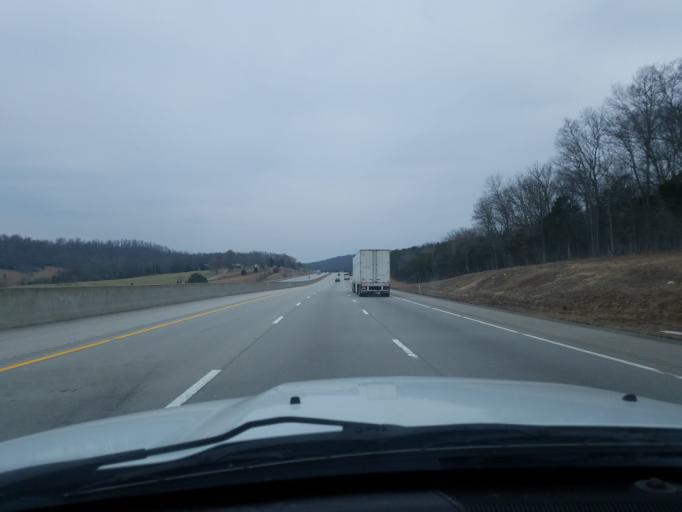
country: US
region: Kentucky
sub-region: Barren County
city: Cave City
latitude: 37.1218
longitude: -86.0012
